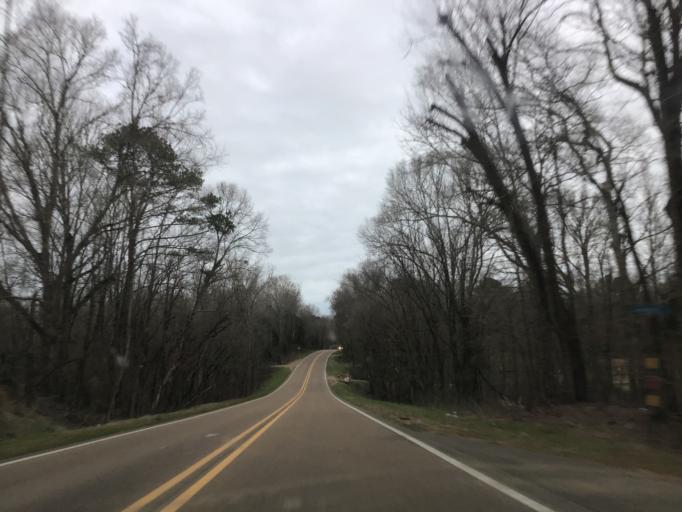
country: US
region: Mississippi
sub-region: Warren County
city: Beechwood
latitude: 32.2824
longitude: -90.7833
